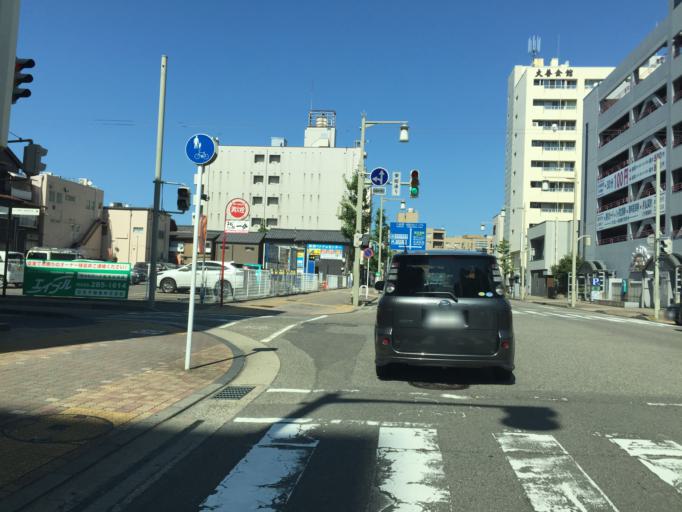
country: JP
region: Niigata
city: Niigata-shi
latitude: 37.9247
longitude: 139.0467
